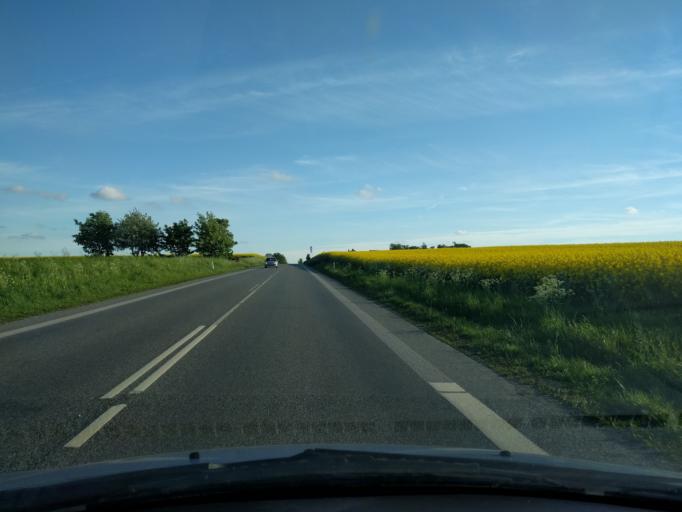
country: DK
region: Zealand
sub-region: Guldborgsund Kommune
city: Stubbekobing
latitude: 54.8763
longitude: 12.0277
